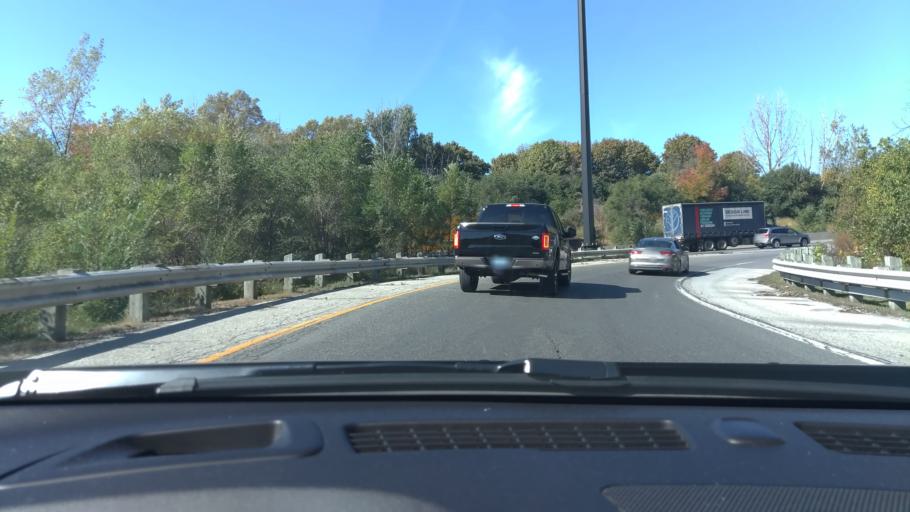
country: CA
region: Ontario
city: Willowdale
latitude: 43.7420
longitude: -79.3313
